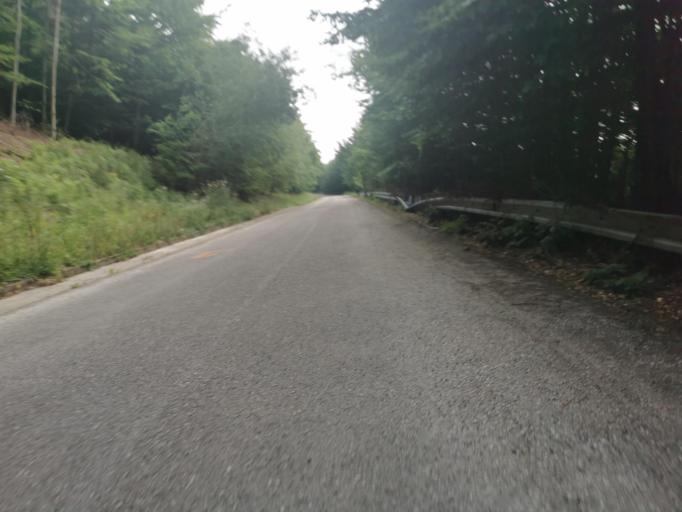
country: SK
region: Trenciansky
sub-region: Okres Myjava
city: Myjava
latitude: 48.8335
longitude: 17.6116
